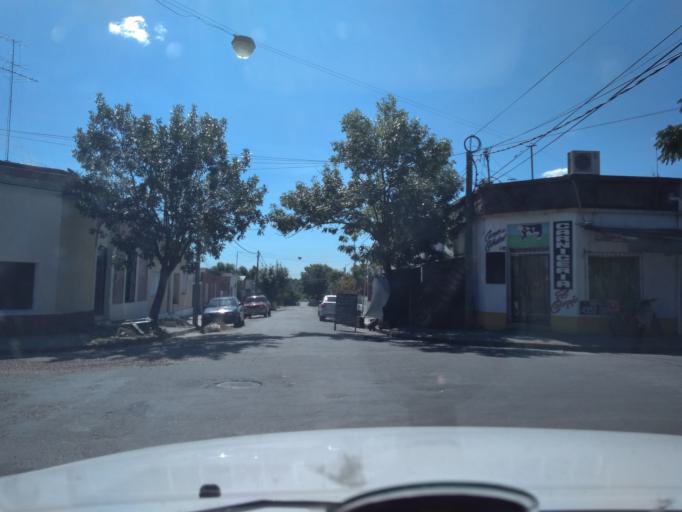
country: UY
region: Florida
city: Florida
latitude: -34.1024
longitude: -56.2200
